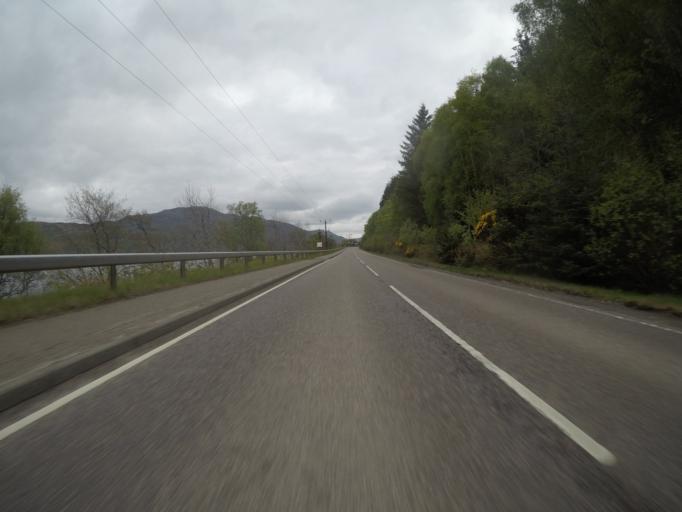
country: GB
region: Scotland
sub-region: Highland
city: Beauly
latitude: 57.2014
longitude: -4.6079
